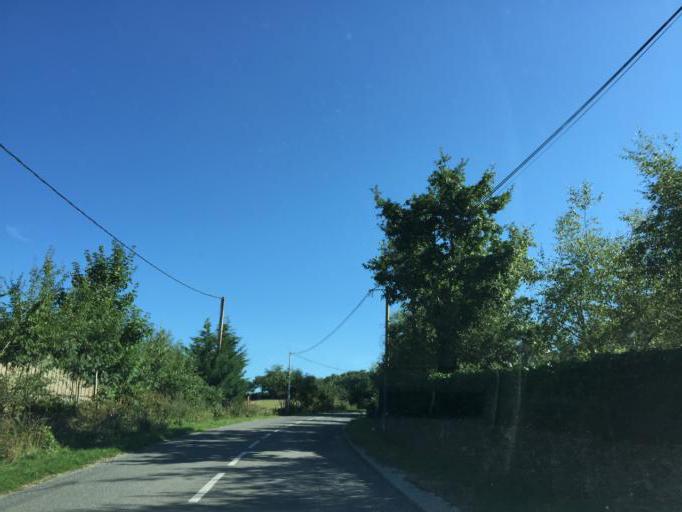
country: FR
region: Midi-Pyrenees
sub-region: Departement de l'Aveyron
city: Pont-de-Salars
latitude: 44.3292
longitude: 2.7629
